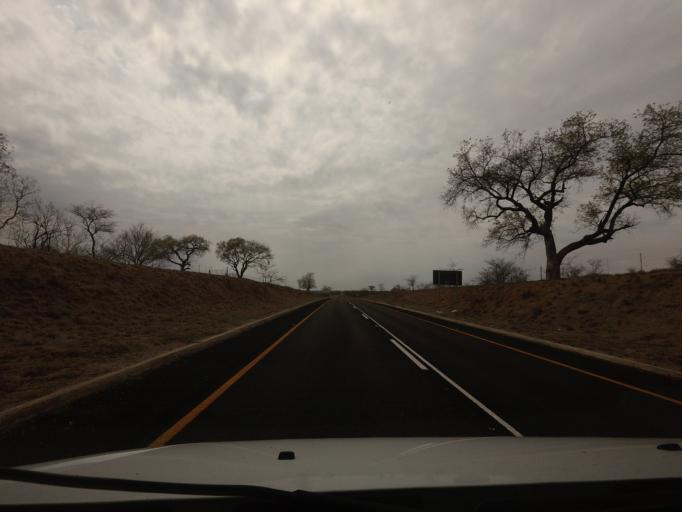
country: ZA
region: Limpopo
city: Thulamahashi
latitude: -24.5558
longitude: 31.2260
